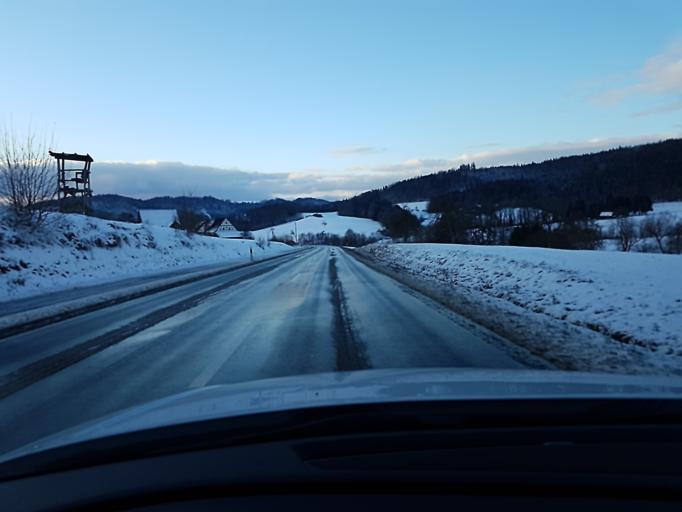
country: DE
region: Baden-Wuerttemberg
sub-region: Regierungsbezirk Stuttgart
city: Fichtenberg
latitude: 48.9808
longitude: 9.6780
